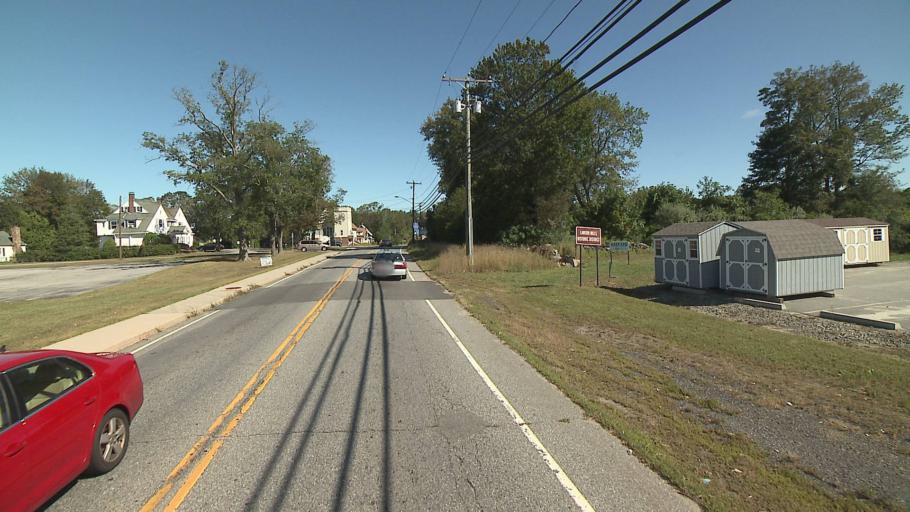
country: US
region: Connecticut
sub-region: Windham County
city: Plainfield
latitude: 41.6760
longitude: -71.9154
